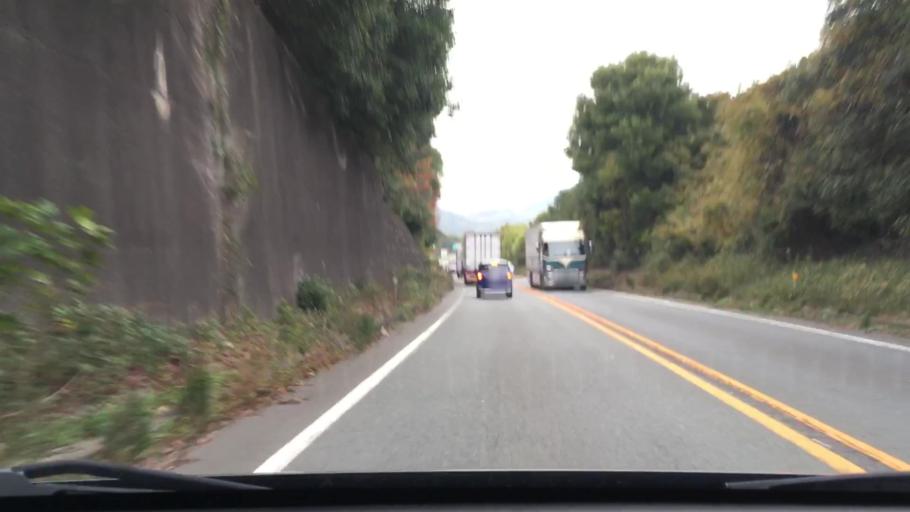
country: JP
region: Yamaguchi
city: Hofu
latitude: 34.0591
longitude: 131.6137
